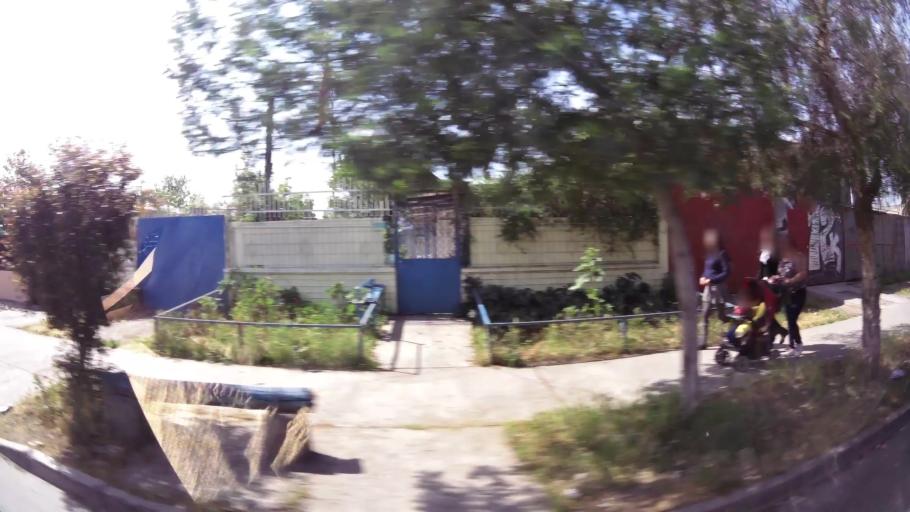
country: CL
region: Santiago Metropolitan
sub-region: Provincia de Santiago
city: Lo Prado
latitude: -33.4380
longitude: -70.7635
